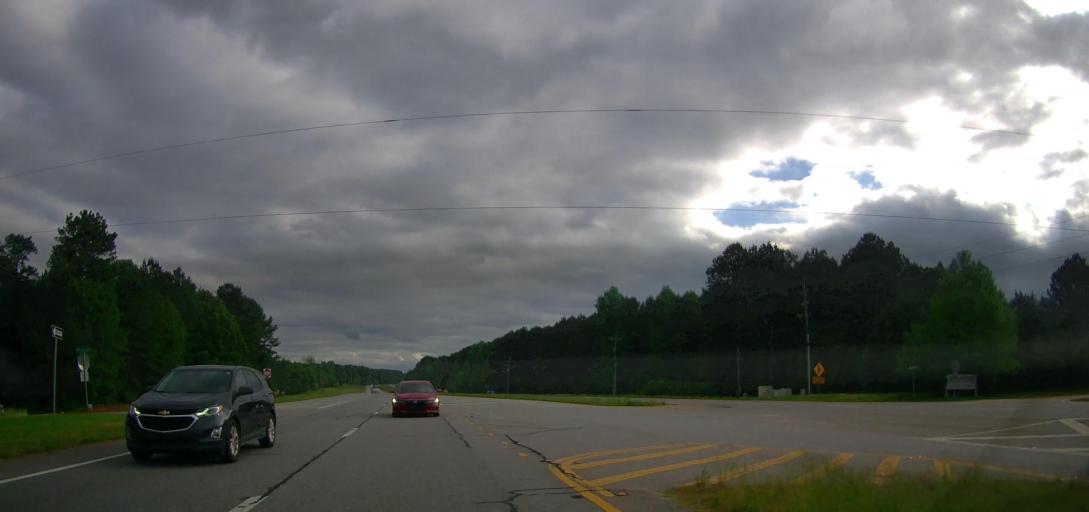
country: US
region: Georgia
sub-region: Barrow County
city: Statham
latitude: 33.8676
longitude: -83.6059
